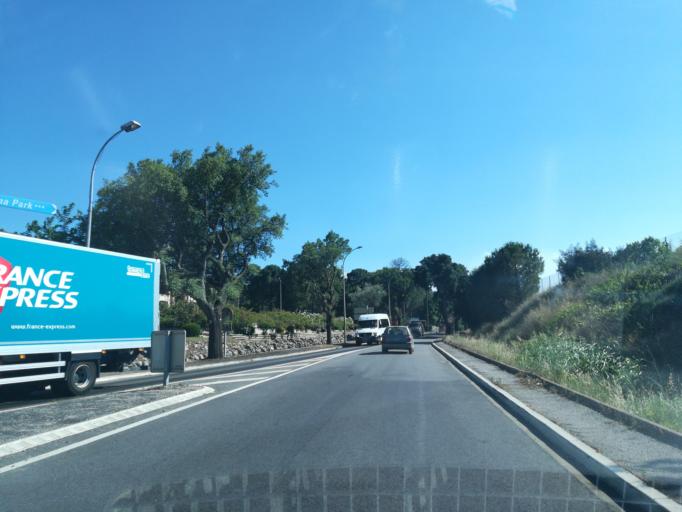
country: FR
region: Languedoc-Roussillon
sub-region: Departement des Pyrenees-Orientales
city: el Volo
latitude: 42.5138
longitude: 2.8299
